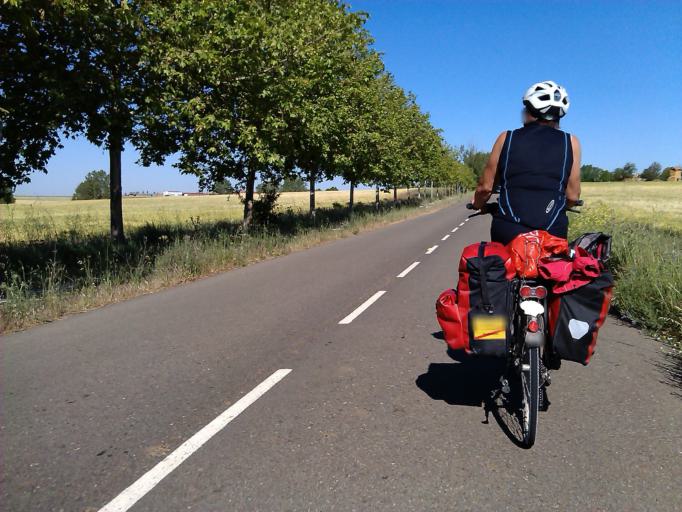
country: ES
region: Castille and Leon
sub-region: Provincia de Leon
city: Bercianos del Real Camino
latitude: 42.3886
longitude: -5.1280
